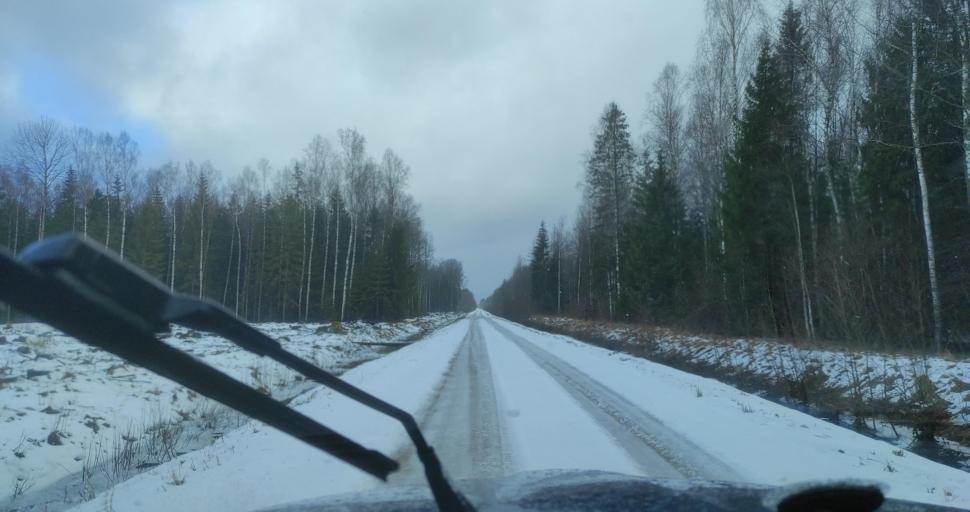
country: LV
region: Dundaga
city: Dundaga
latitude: 57.3924
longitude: 22.1275
